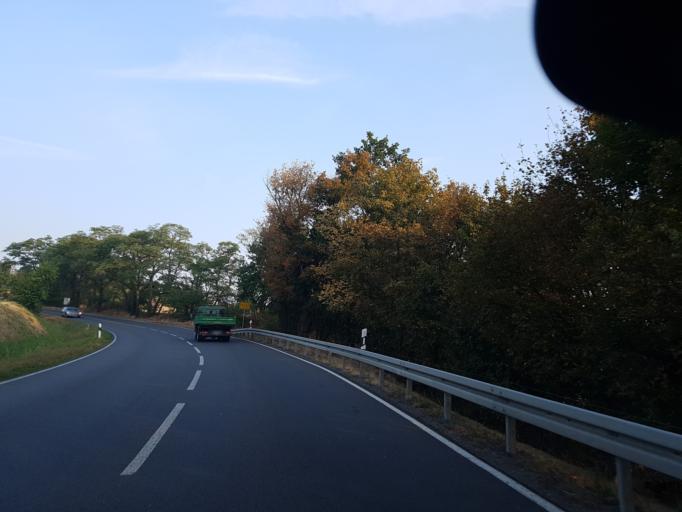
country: DE
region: Saxony
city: Dommitzsch
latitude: 51.6363
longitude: 12.8910
